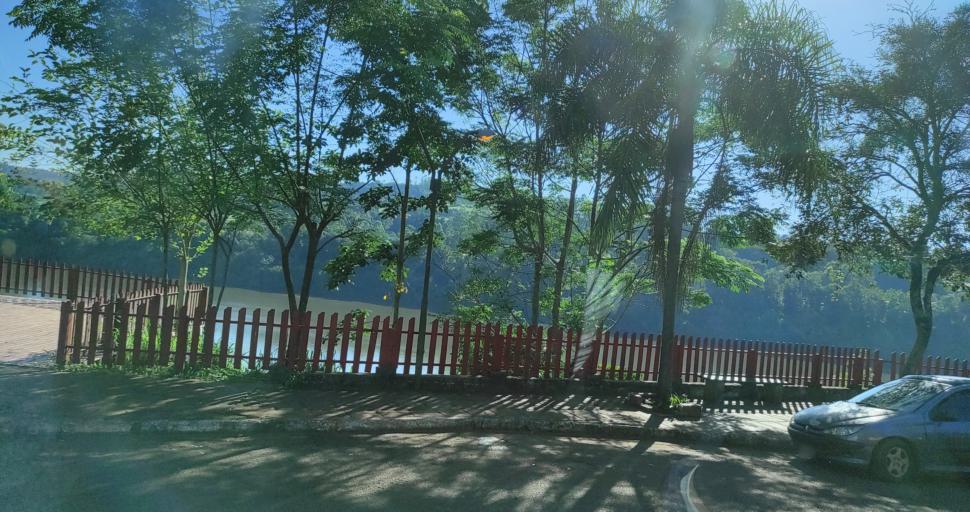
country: AR
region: Misiones
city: El Soberbio
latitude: -27.2974
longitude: -54.1941
